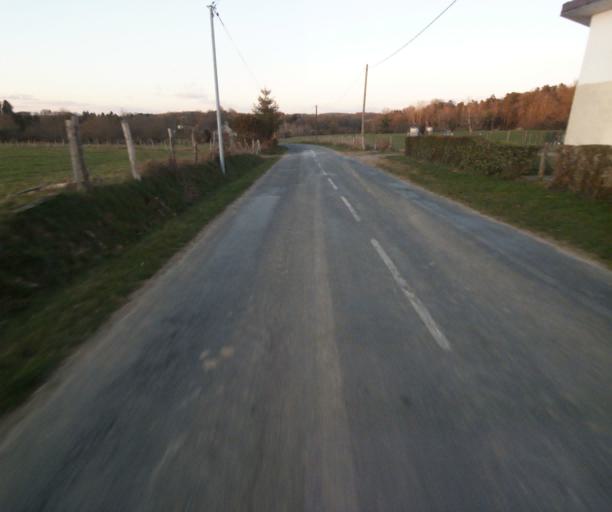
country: FR
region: Limousin
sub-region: Departement de la Correze
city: Saint-Mexant
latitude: 45.3367
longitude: 1.6158
